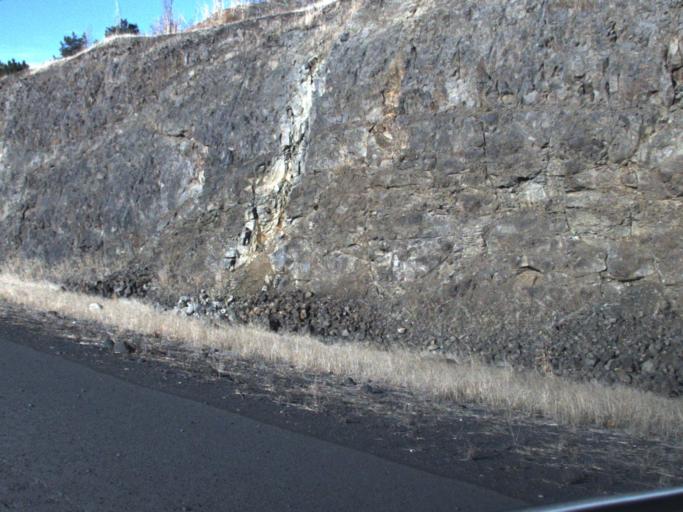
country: US
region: Washington
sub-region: Whitman County
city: Pullman
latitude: 46.7280
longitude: -117.1076
